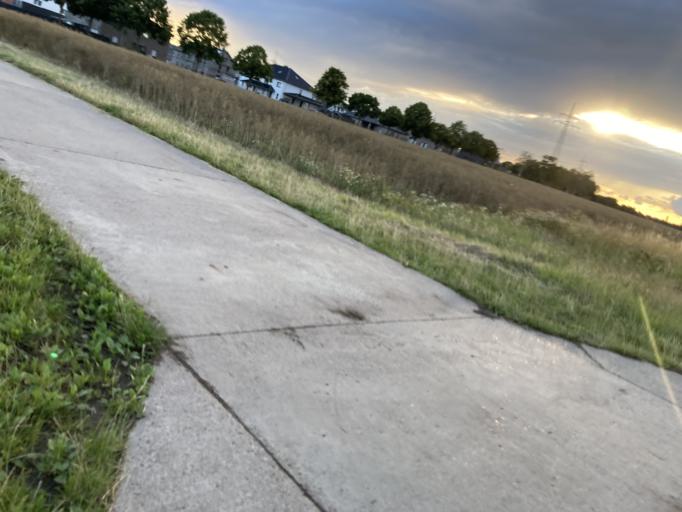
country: DE
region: Lower Saxony
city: Verden
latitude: 52.9264
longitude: 9.2150
